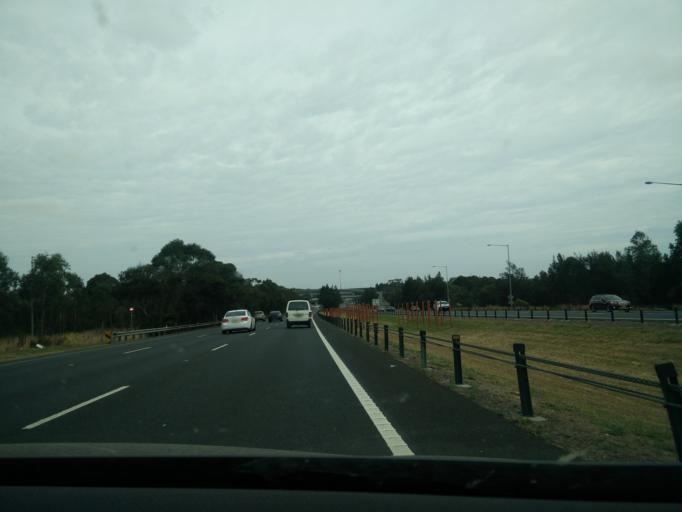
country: AU
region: New South Wales
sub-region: Blacktown
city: Doonside
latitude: -33.8004
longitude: 150.8651
